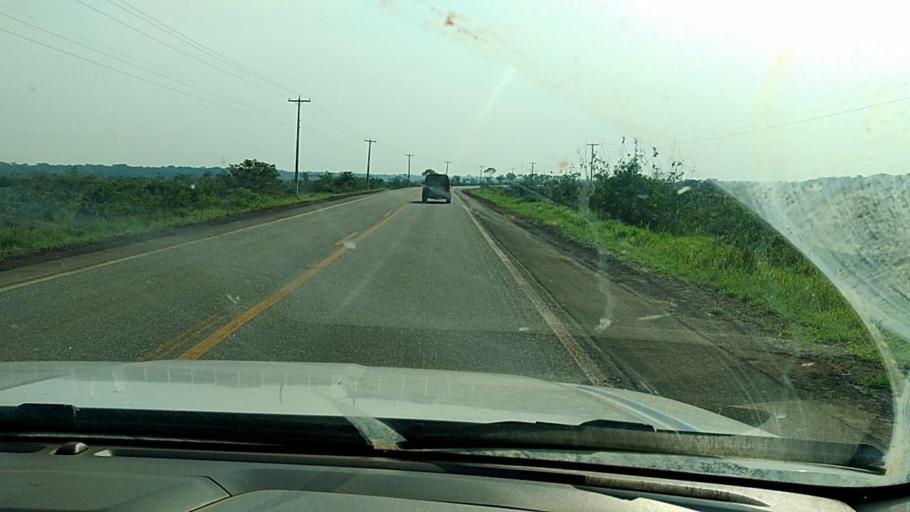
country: BR
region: Rondonia
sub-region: Porto Velho
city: Porto Velho
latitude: -8.1487
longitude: -63.7738
